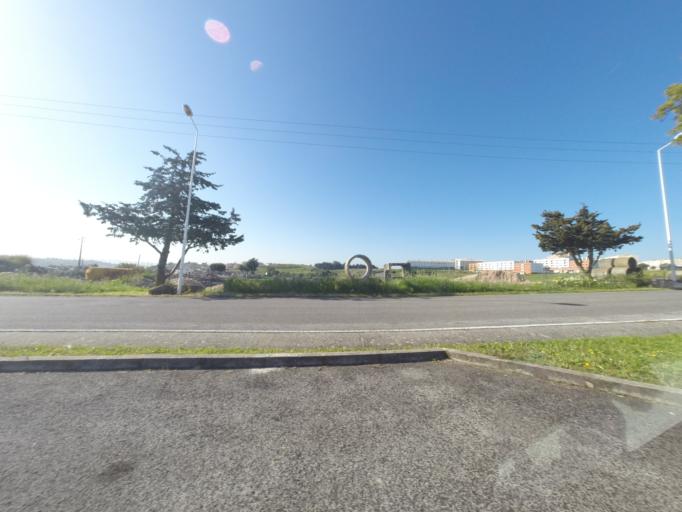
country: PT
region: Lisbon
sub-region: Oeiras
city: Terrugem
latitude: 38.7129
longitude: -9.2854
